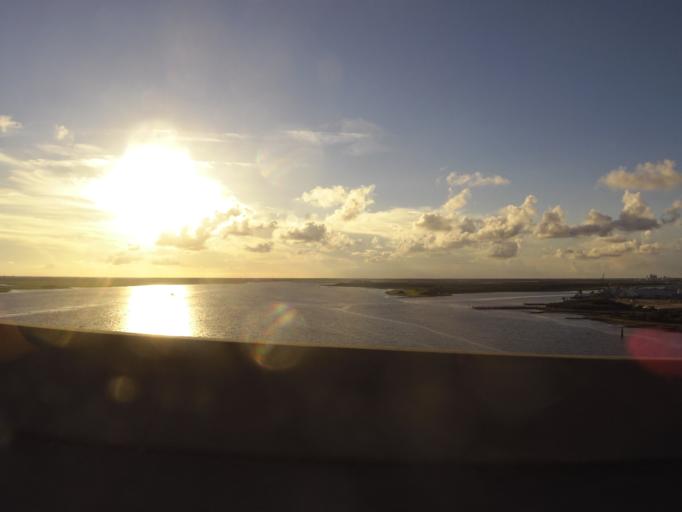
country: US
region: Georgia
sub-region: Glynn County
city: Brunswick
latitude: 31.1199
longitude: -81.4834
